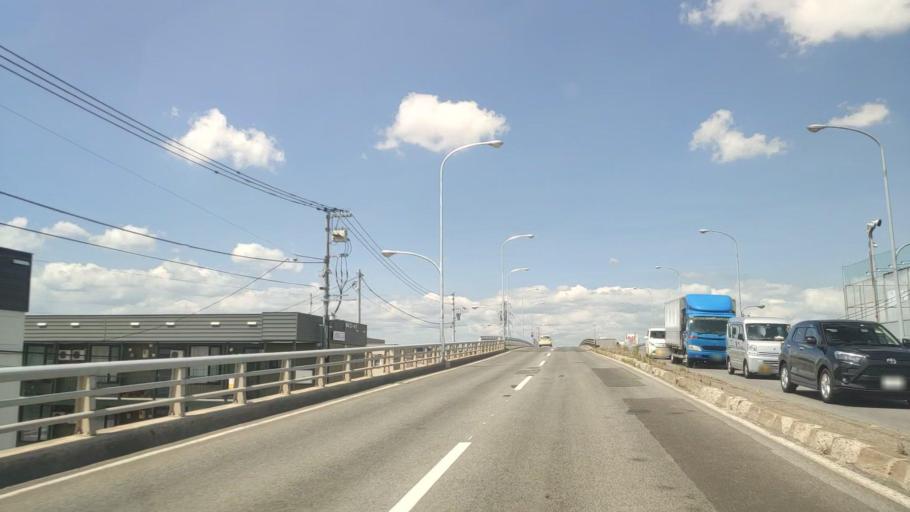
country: JP
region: Hokkaido
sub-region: Asahikawa-shi
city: Asahikawa
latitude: 43.7926
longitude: 142.4024
